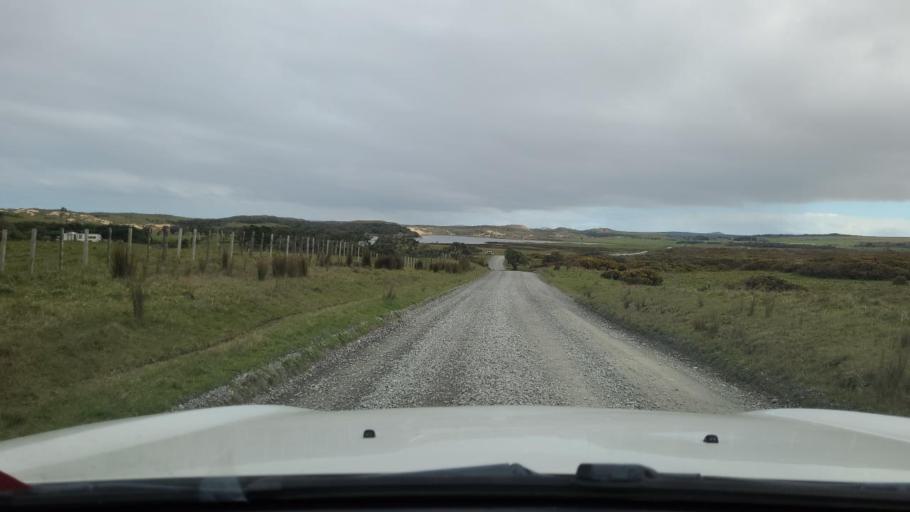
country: NZ
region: Chatham Islands
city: Waitangi
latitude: -43.8271
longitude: -176.5605
